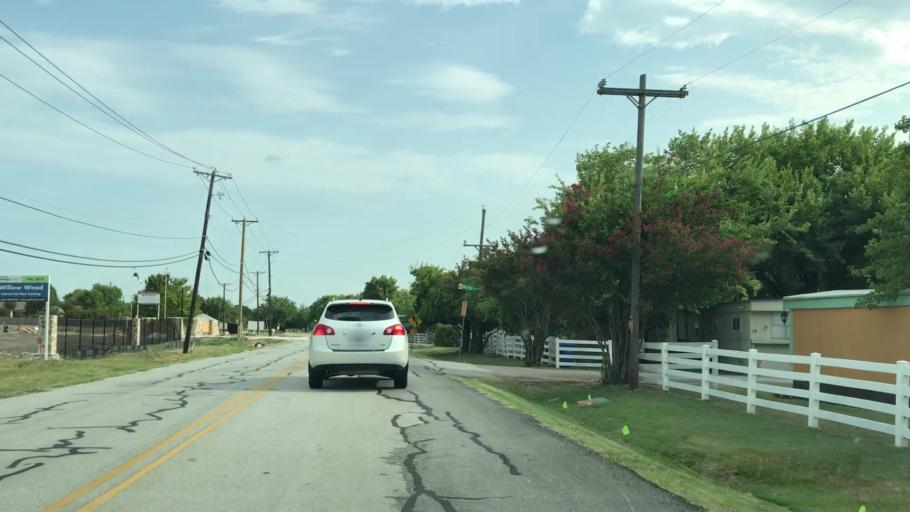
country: US
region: Texas
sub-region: Dallas County
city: Rowlett
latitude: 32.9273
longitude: -96.5364
